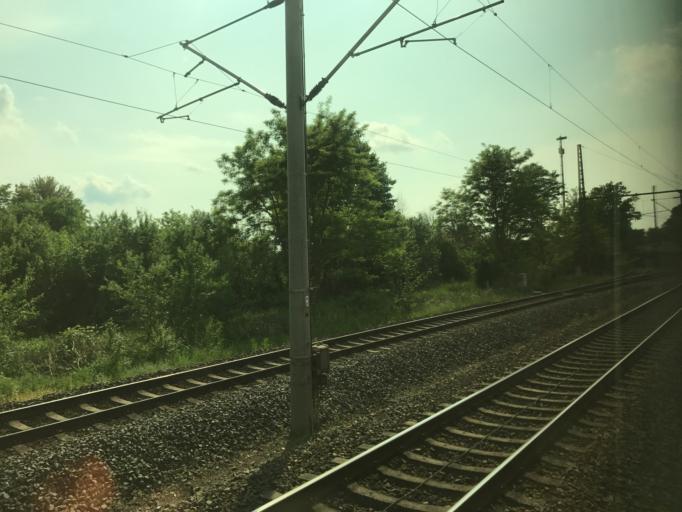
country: DE
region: Brandenburg
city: Nennhausen
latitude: 52.5997
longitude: 12.5035
